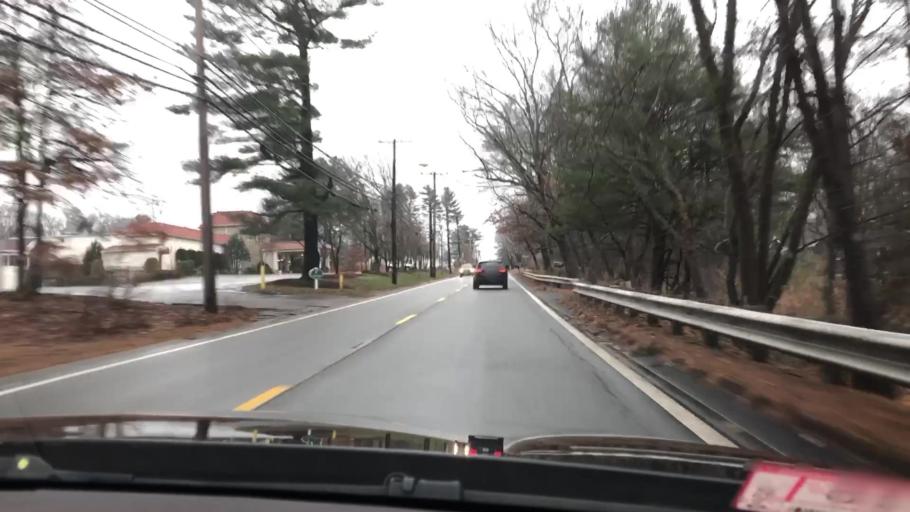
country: US
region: Massachusetts
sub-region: Norfolk County
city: Walpole
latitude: 42.1254
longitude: -71.2695
